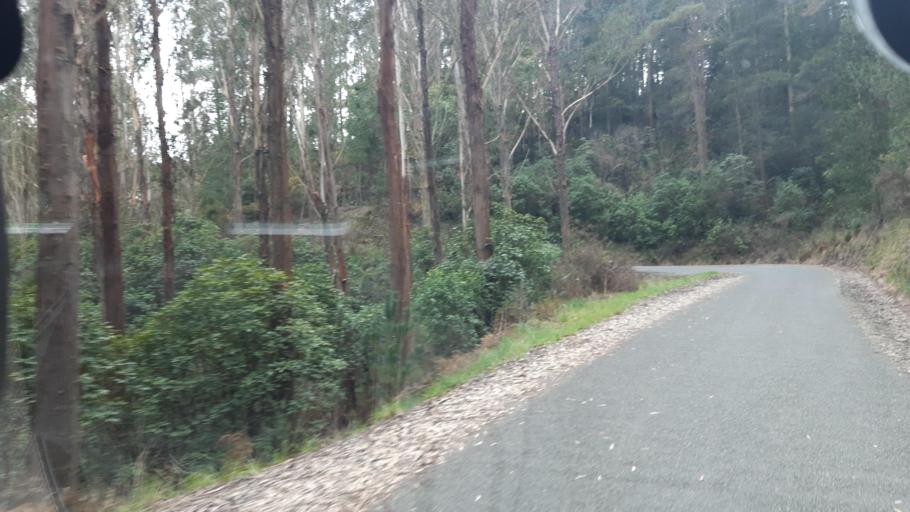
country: NZ
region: Tasman
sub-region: Tasman District
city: Motueka
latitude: -41.2664
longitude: 172.8876
